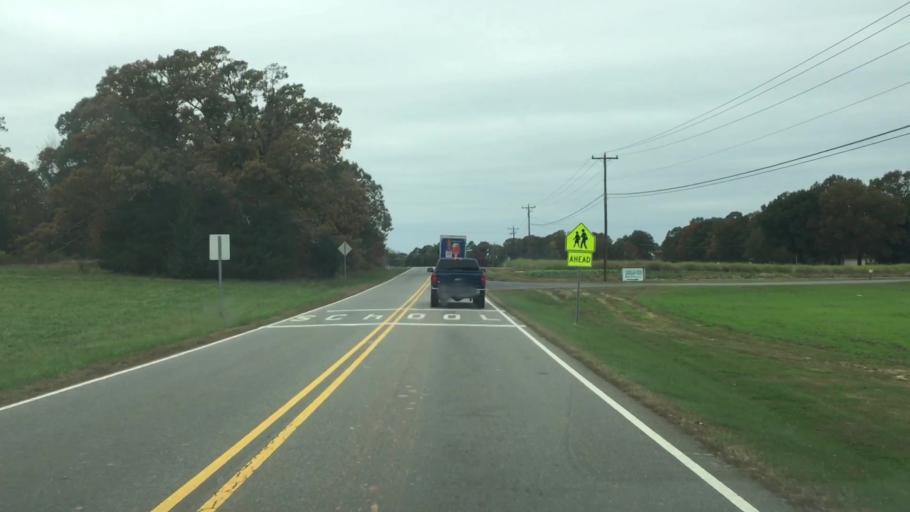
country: US
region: North Carolina
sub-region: Iredell County
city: Mooresville
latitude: 35.6008
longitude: -80.7705
